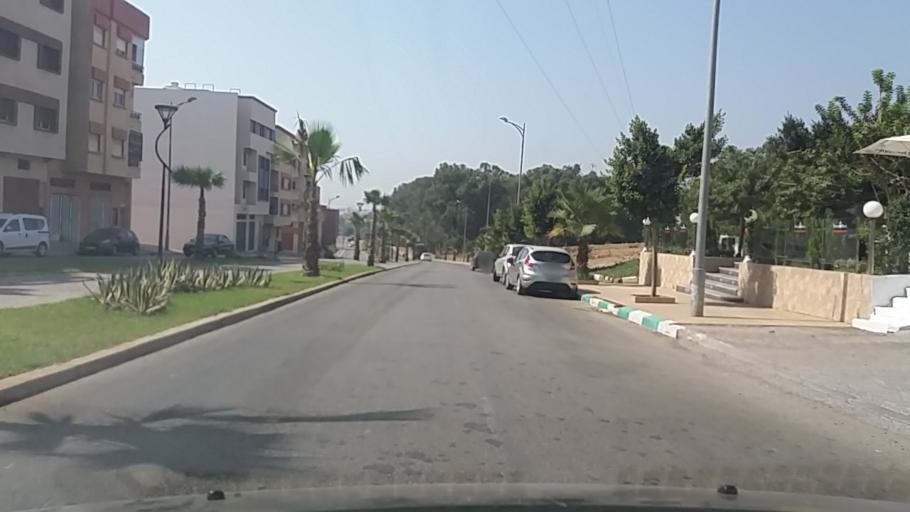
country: MA
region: Gharb-Chrarda-Beni Hssen
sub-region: Kenitra Province
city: Kenitra
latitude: 34.2522
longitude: -6.6149
